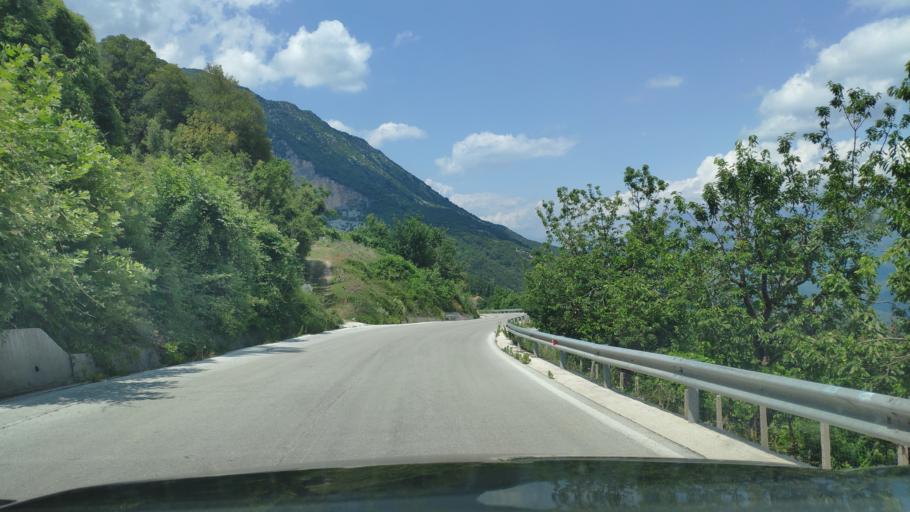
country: GR
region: Epirus
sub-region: Nomos Artas
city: Agios Dimitrios
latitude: 39.3375
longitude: 21.0059
